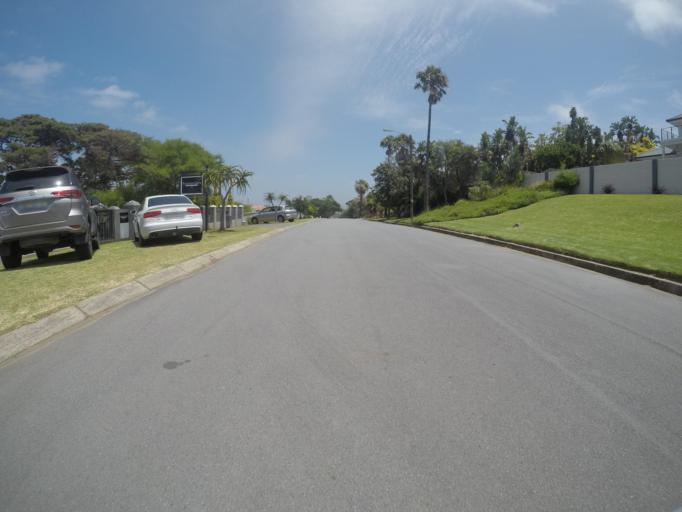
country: ZA
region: Eastern Cape
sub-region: Buffalo City Metropolitan Municipality
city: East London
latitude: -32.9989
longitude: 27.9299
